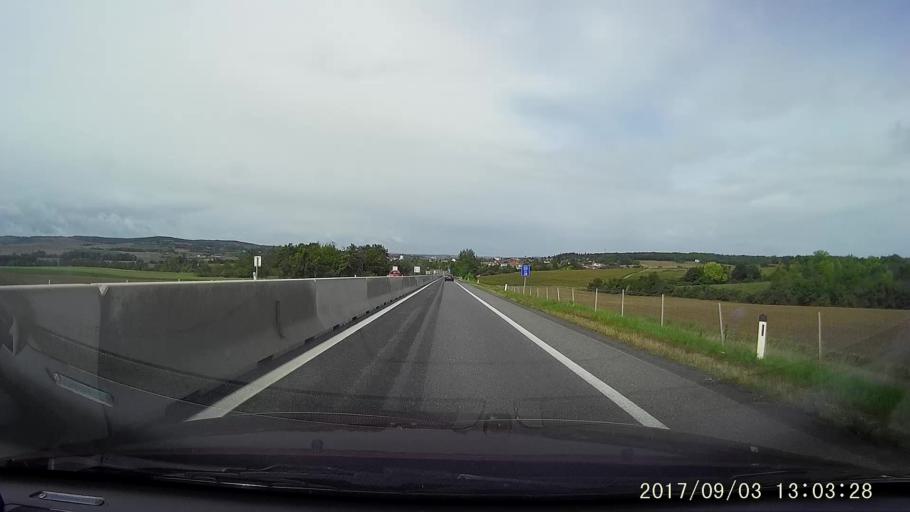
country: AT
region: Lower Austria
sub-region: Politischer Bezirk Hollabrunn
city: Hollabrunn
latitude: 48.5358
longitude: 16.0809
